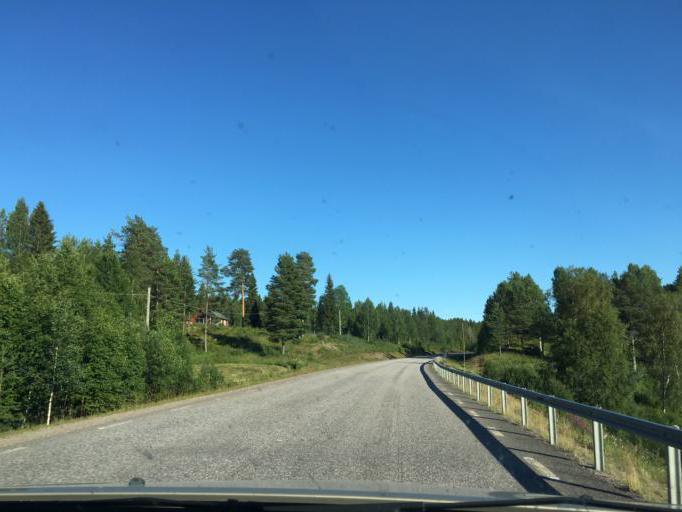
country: SE
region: Norrbotten
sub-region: Kalix Kommun
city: Rolfs
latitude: 65.9159
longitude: 22.9220
